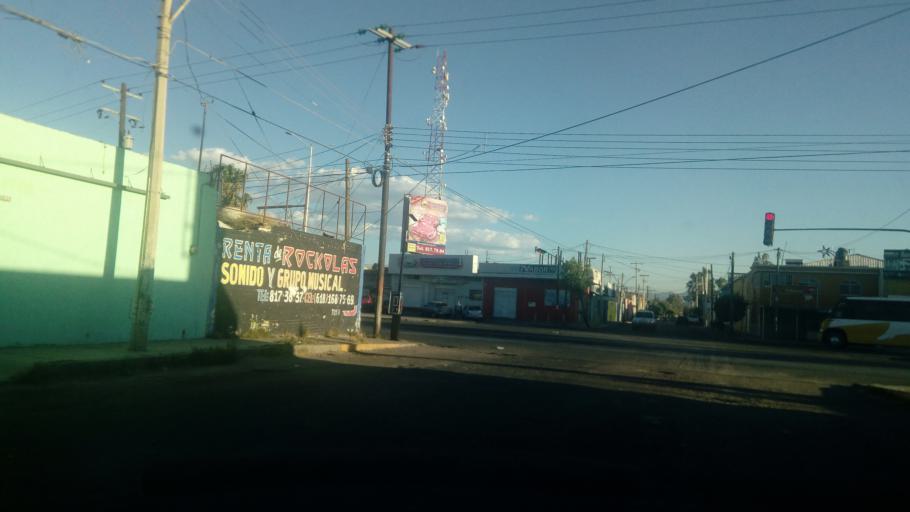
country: MX
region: Durango
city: Victoria de Durango
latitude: 24.0328
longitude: -104.6321
